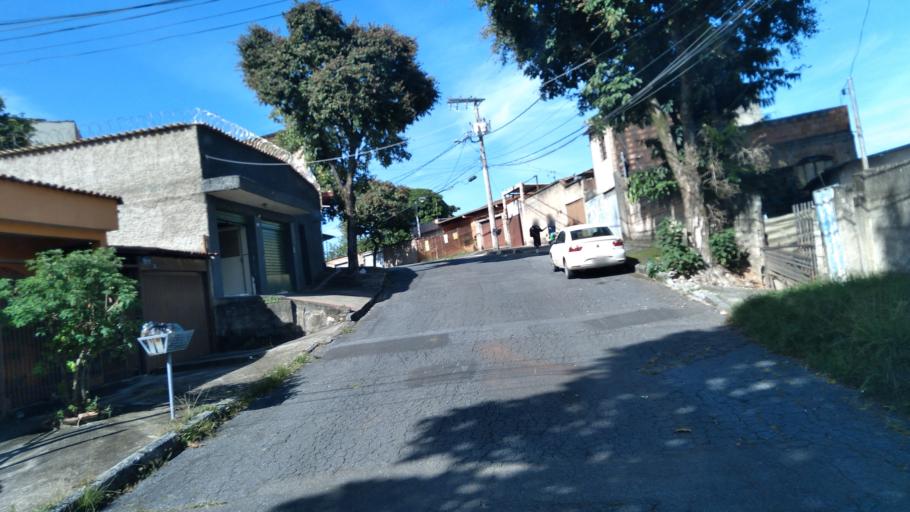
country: BR
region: Minas Gerais
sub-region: Contagem
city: Contagem
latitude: -19.9062
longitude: -44.0011
